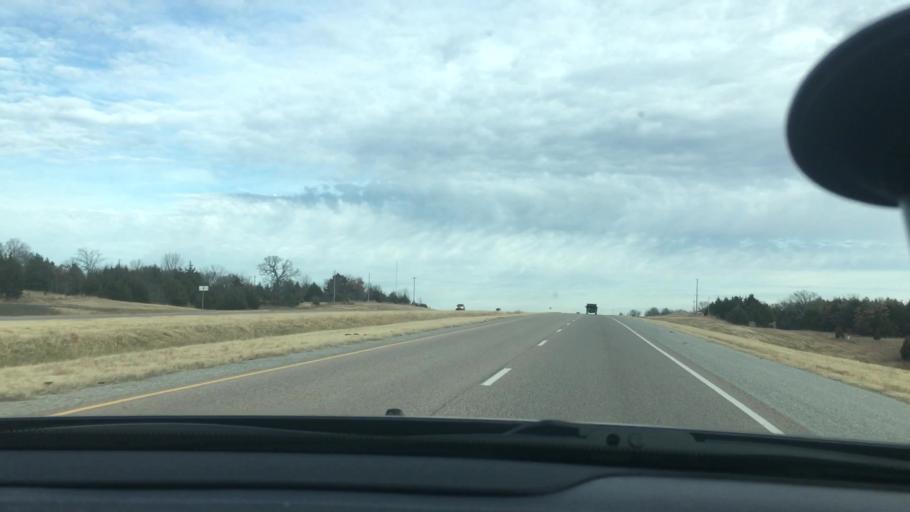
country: US
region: Oklahoma
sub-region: Pontotoc County
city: Byng
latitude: 34.8710
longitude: -96.6786
